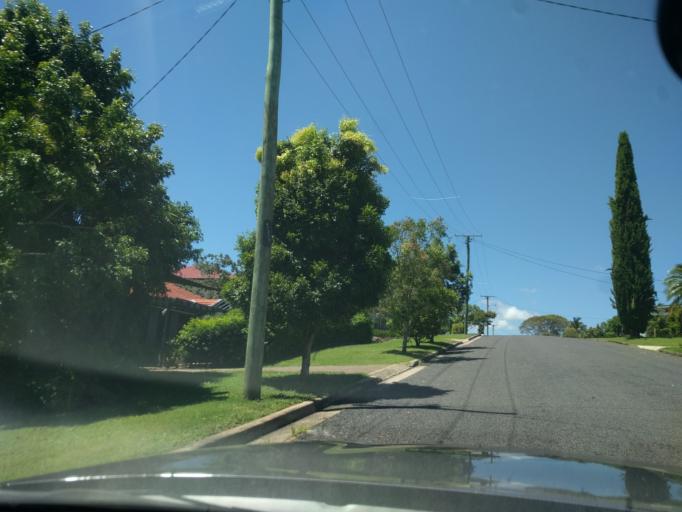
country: AU
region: Queensland
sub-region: Logan
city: Cedar Vale
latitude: -27.9851
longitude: 153.0042
